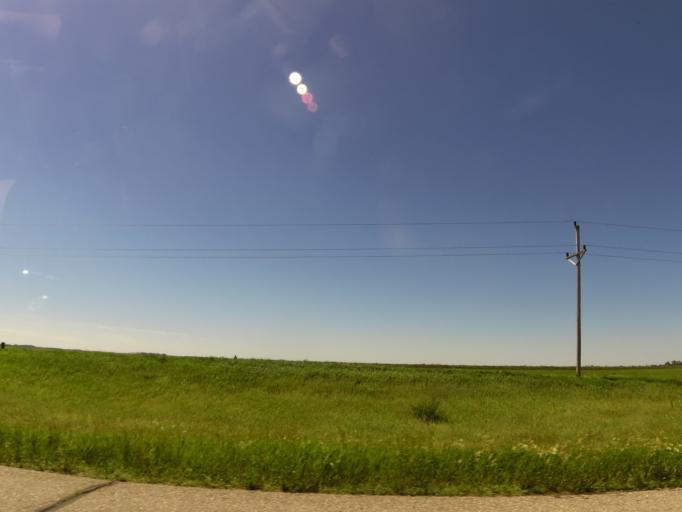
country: US
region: Minnesota
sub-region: Red Lake County
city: Red Lake Falls
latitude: 47.7602
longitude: -96.3210
